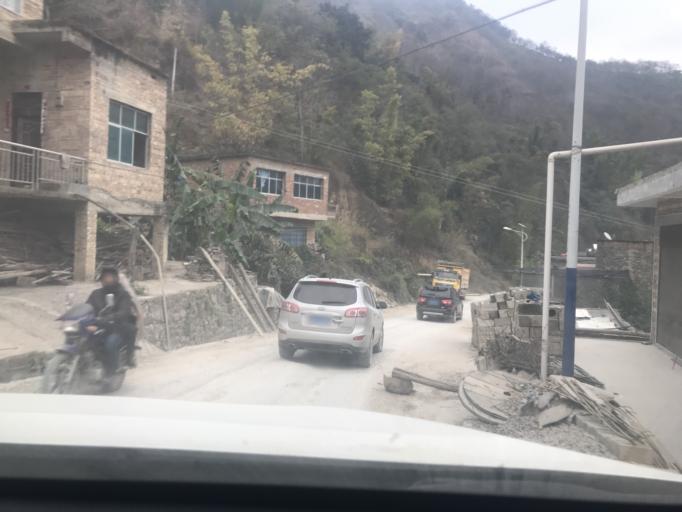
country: CN
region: Guangxi Zhuangzu Zizhiqu
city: Xinzhou
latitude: 25.0282
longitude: 105.8616
